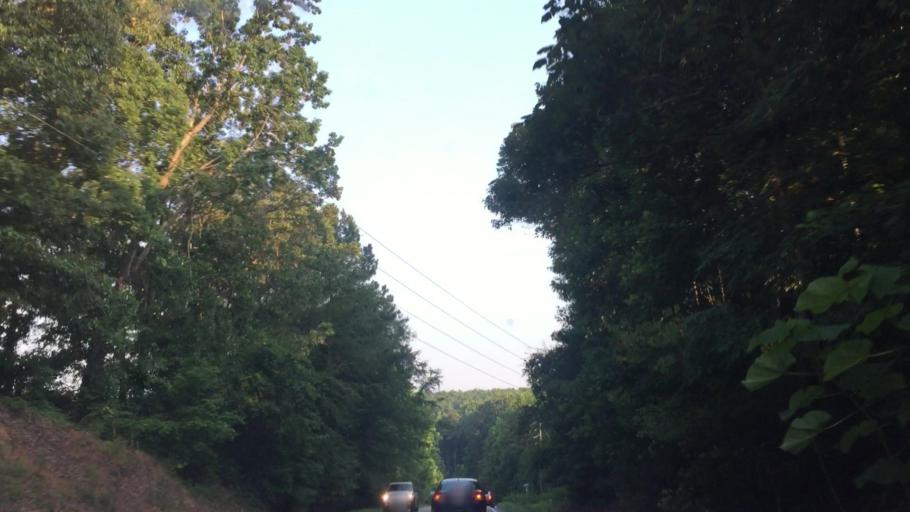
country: US
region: Georgia
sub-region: DeKalb County
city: Pine Mountain
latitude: 33.6339
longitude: -84.1835
